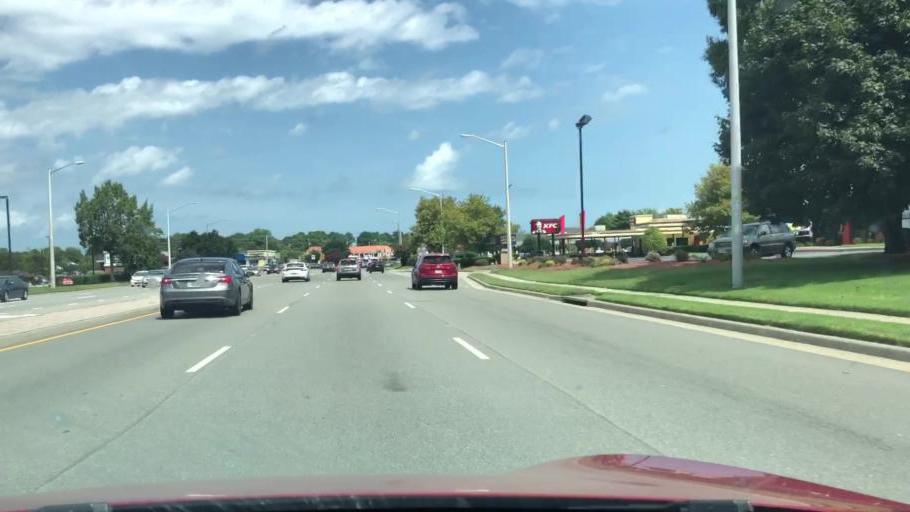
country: US
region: Virginia
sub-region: City of Chesapeake
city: Chesapeake
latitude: 36.8720
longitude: -76.1339
